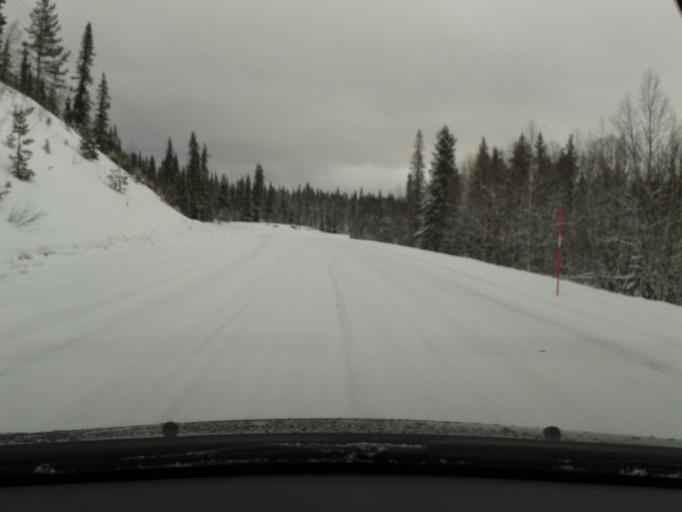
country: SE
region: Vaesterbotten
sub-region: Vilhelmina Kommun
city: Sjoberg
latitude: 65.2408
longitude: 15.7768
